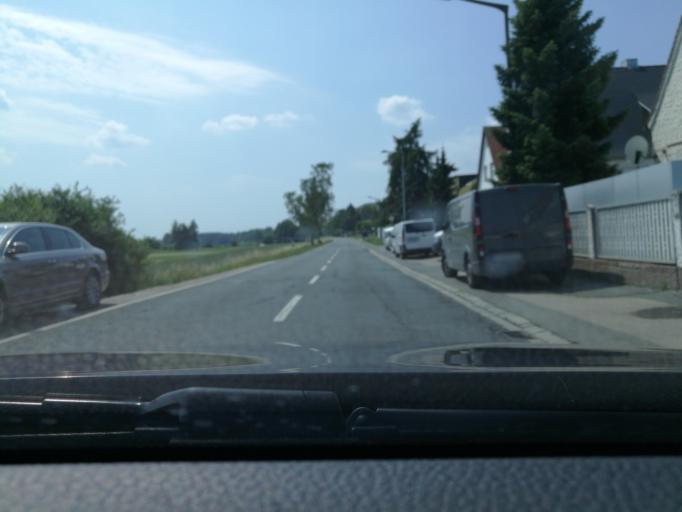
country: DE
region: Bavaria
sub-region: Regierungsbezirk Mittelfranken
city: Furth
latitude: 49.5189
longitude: 10.9643
